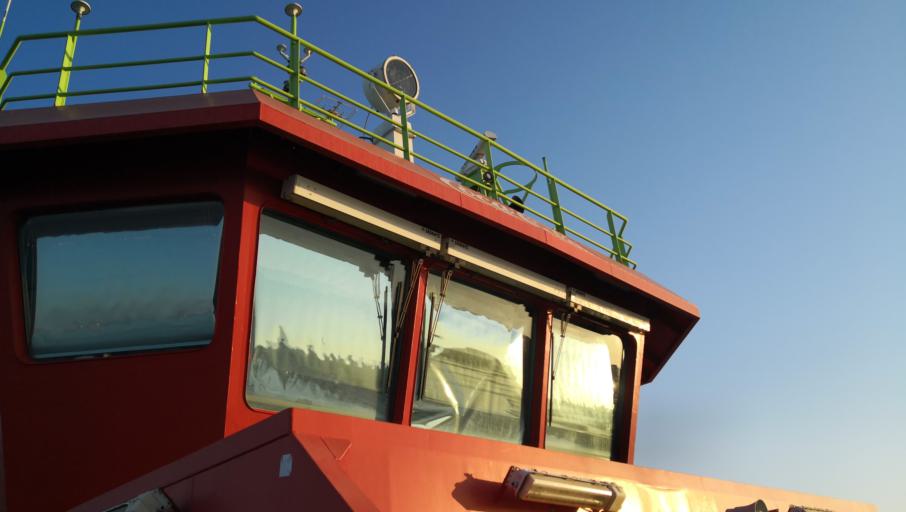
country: PT
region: Setubal
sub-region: Setubal
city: Setubal
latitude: 38.4678
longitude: -8.8634
